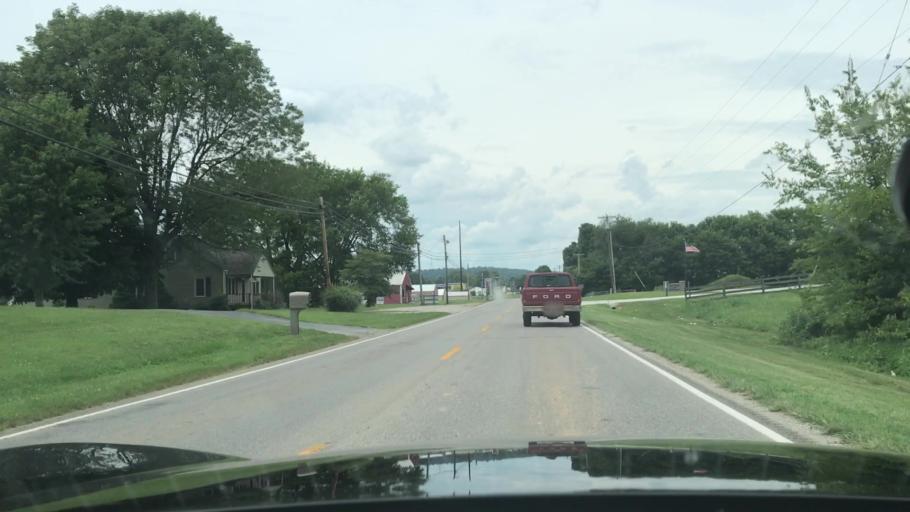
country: US
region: Kentucky
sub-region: Hart County
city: Horse Cave
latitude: 37.1777
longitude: -85.8850
